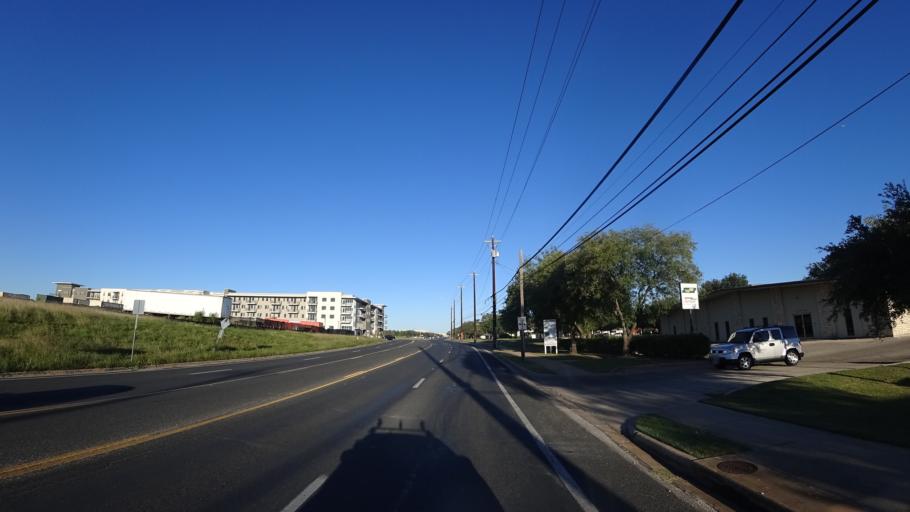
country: US
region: Texas
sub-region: Travis County
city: Austin
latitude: 30.3043
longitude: -97.6996
